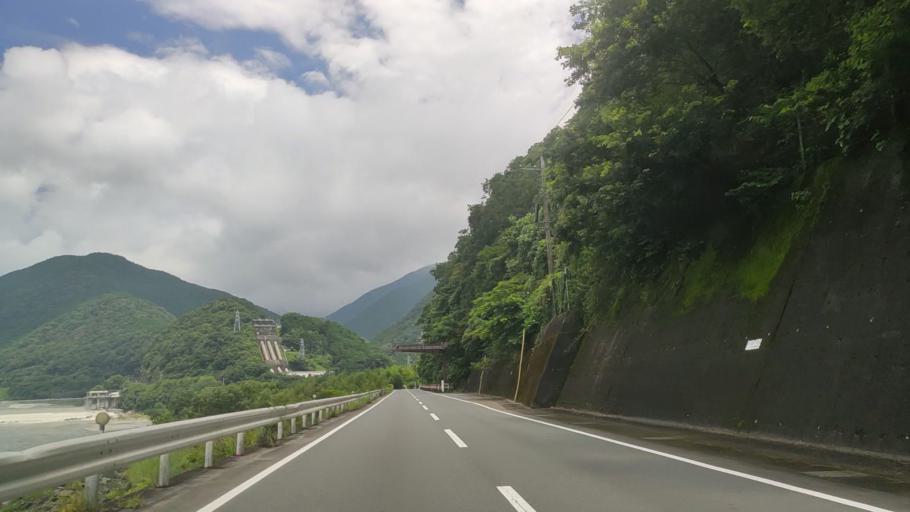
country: JP
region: Shizuoka
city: Fujinomiya
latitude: 35.2334
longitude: 138.5108
